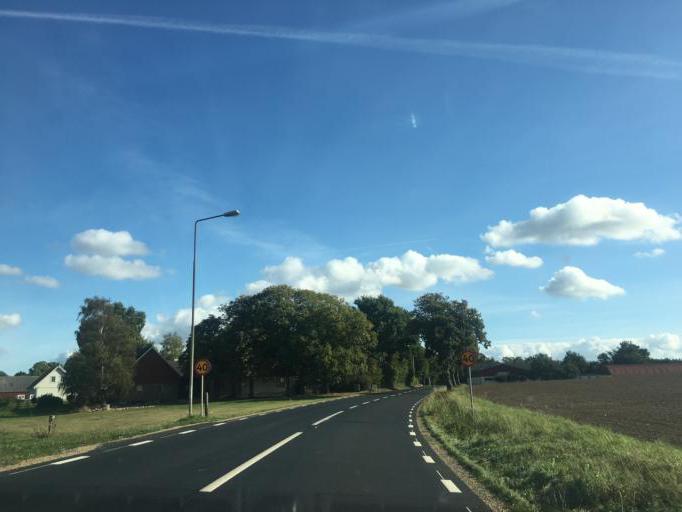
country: SE
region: Skane
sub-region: Kavlinge Kommun
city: Loddekopinge
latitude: 55.8168
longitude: 13.0442
